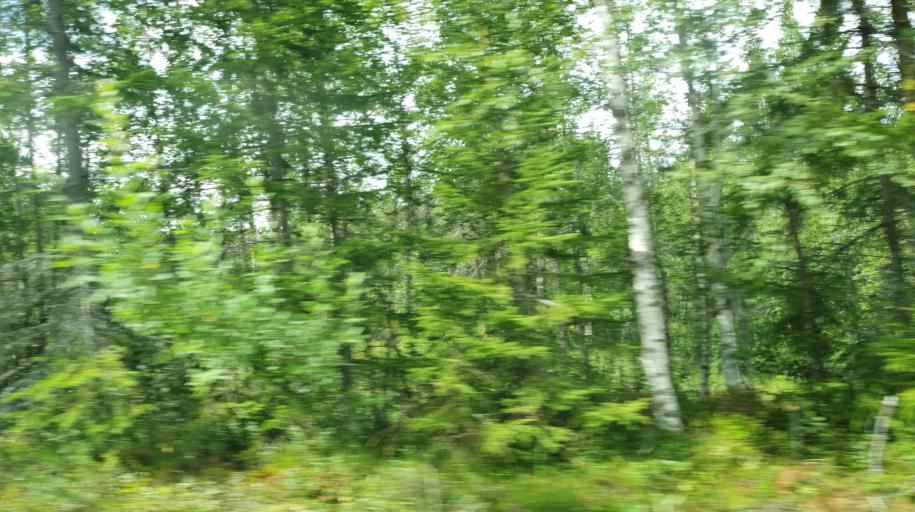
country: NO
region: Nord-Trondelag
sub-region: Levanger
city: Skogn
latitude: 63.5795
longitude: 11.2444
